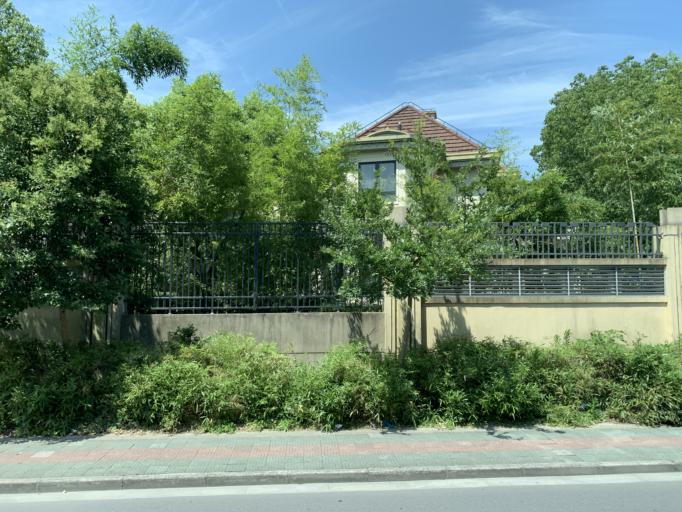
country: CN
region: Shanghai Shi
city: Huamu
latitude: 31.1779
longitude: 121.5342
